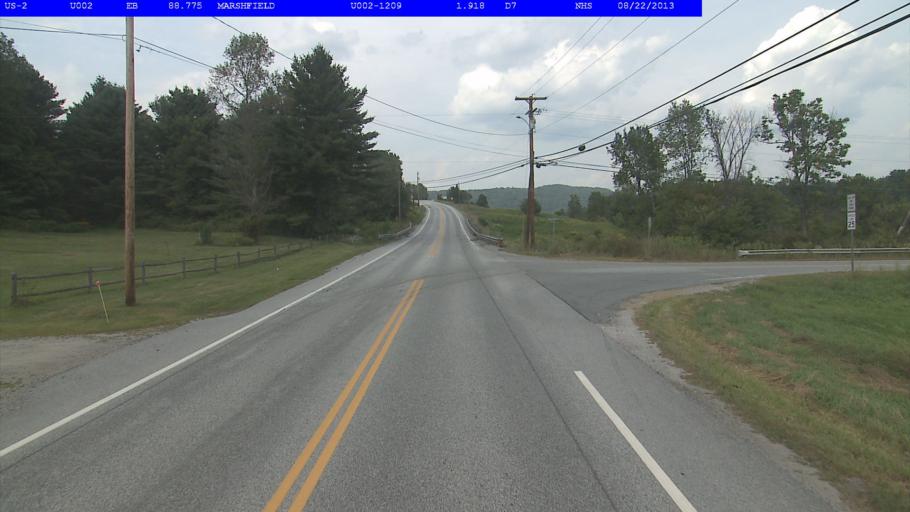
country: US
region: Vermont
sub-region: Washington County
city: Barre
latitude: 44.2986
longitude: -72.3983
